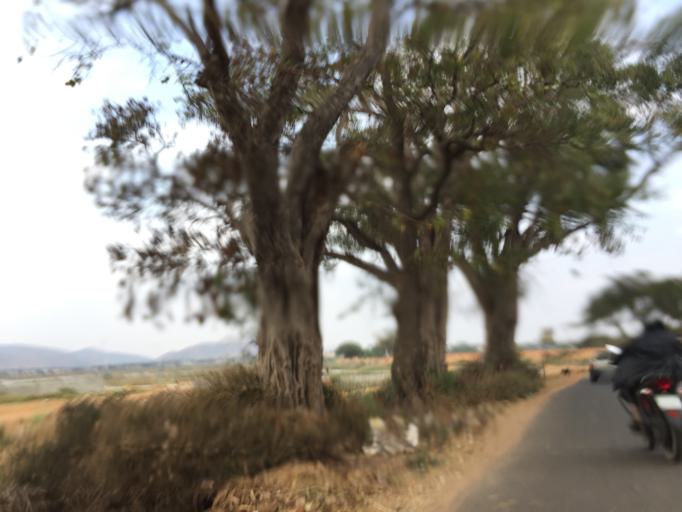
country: IN
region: Karnataka
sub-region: Chikkaballapur
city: Chik Ballapur
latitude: 13.4168
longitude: 77.7191
